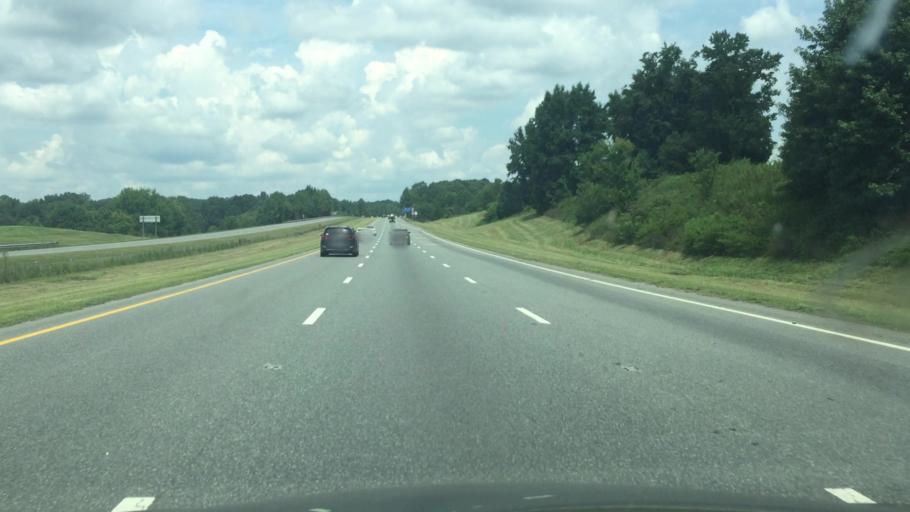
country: US
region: North Carolina
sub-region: Montgomery County
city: Biscoe
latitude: 35.4945
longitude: -79.7801
